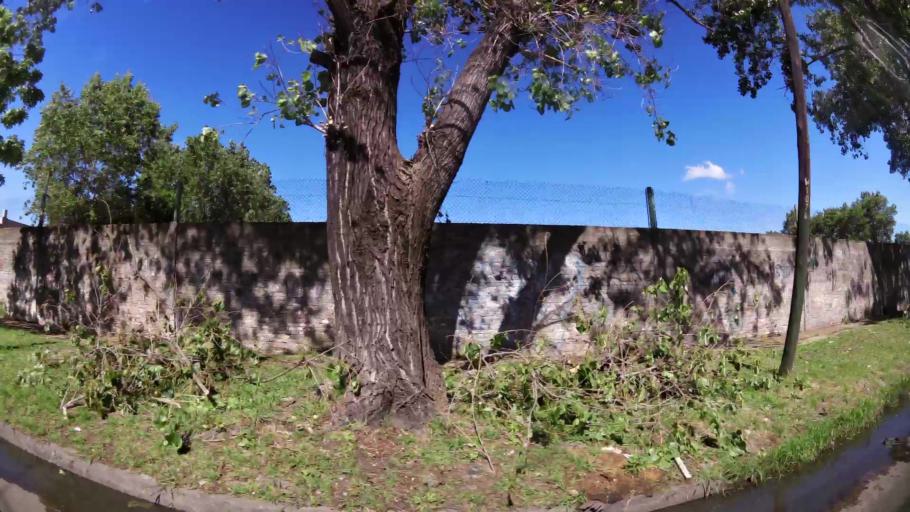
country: AR
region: Buenos Aires
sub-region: Partido de Lomas de Zamora
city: Lomas de Zamora
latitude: -34.7488
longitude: -58.4179
